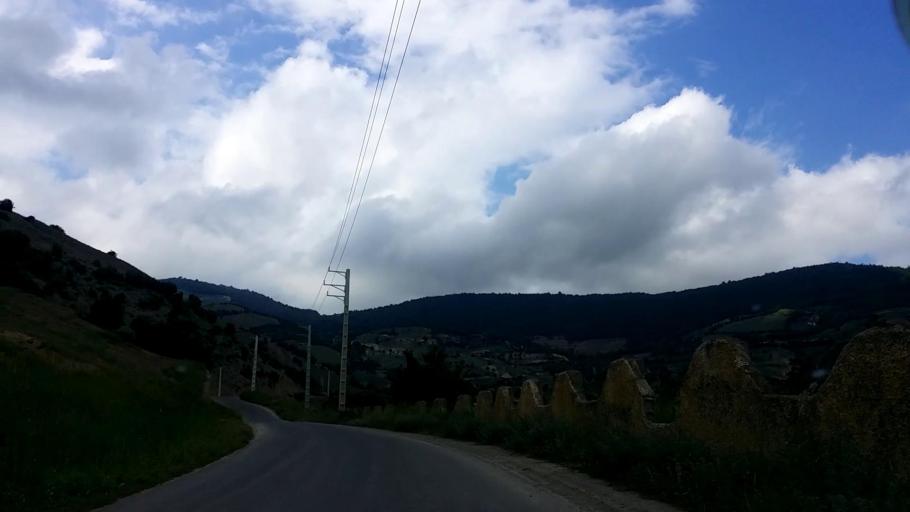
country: IR
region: Mazandaran
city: Chalus
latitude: 36.5455
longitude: 51.2713
